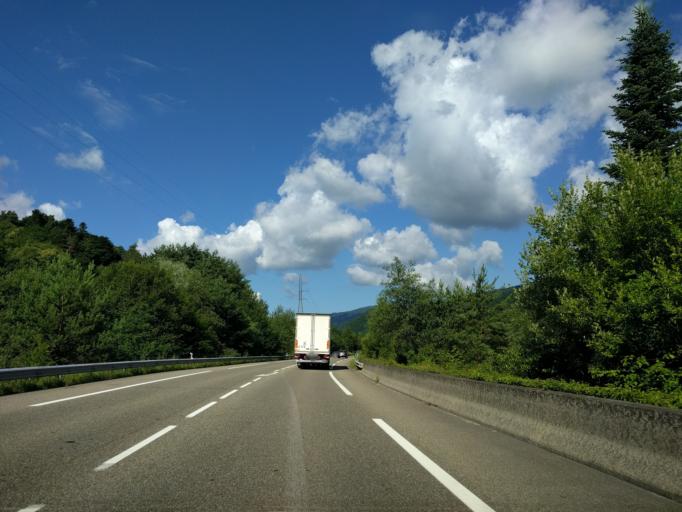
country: FR
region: Alsace
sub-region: Departement du Haut-Rhin
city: Liepvre
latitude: 48.2690
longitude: 7.2732
